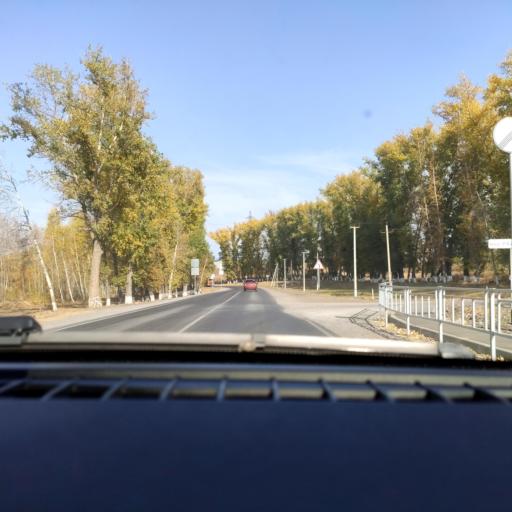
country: RU
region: Voronezj
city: Novaya Usman'
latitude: 51.6730
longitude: 39.4067
